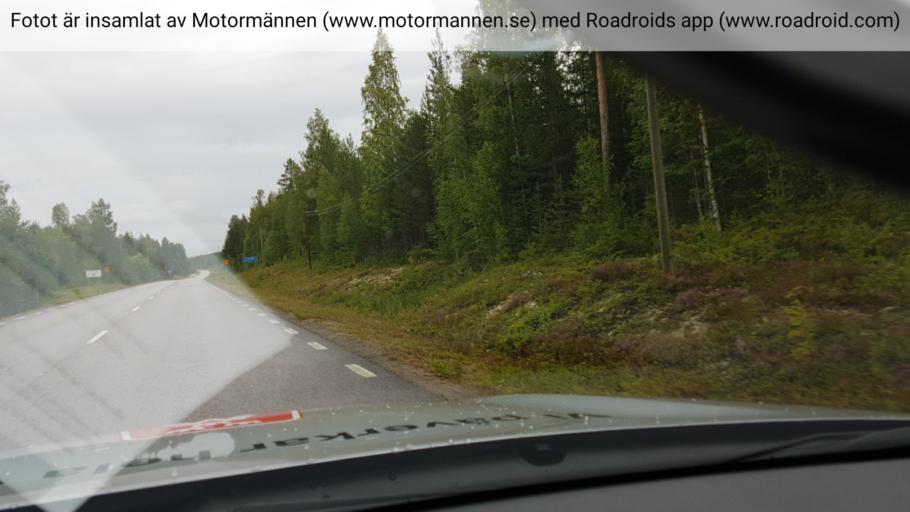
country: SE
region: Norrbotten
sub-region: Alvsbyns Kommun
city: AElvsbyn
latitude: 66.1110
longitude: 20.9307
